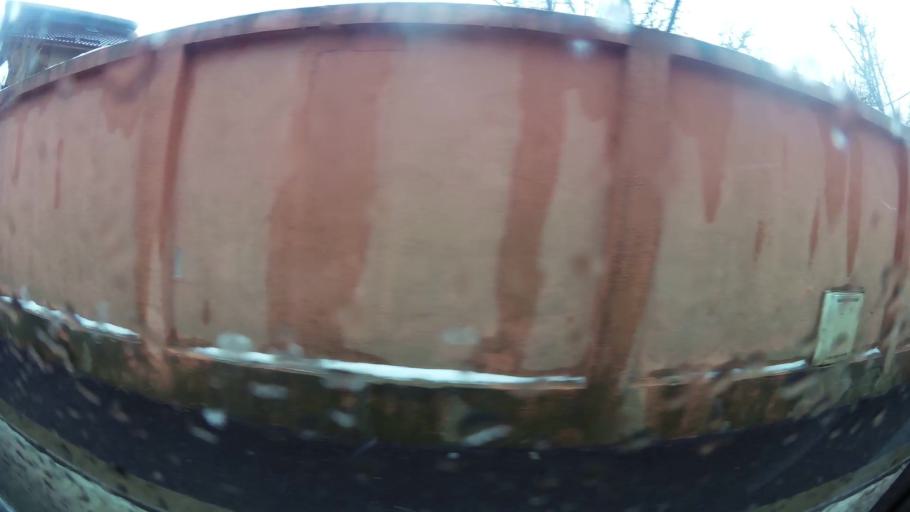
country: RO
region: Ilfov
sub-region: Comuna Chiajna
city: Rosu
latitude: 44.4044
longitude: 26.0113
